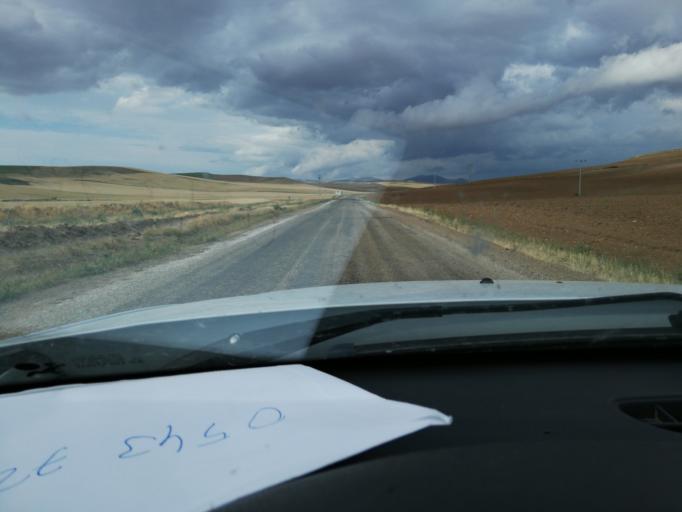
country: TR
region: Kirsehir
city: Kirsehir
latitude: 39.0380
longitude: 34.1473
